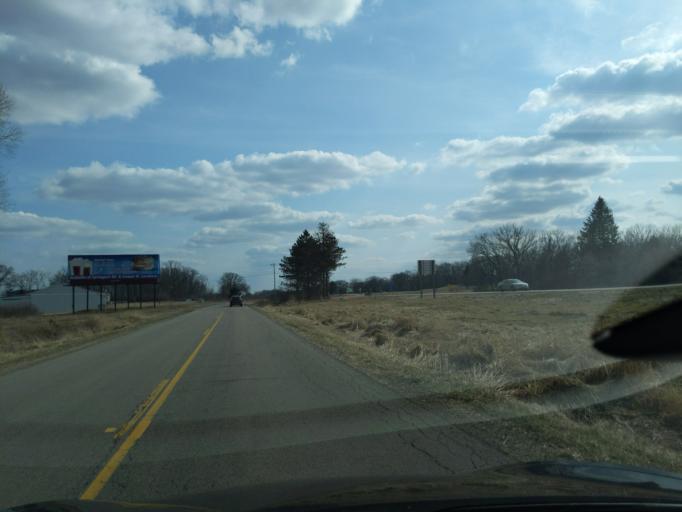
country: US
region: Michigan
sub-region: Ingham County
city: Leslie
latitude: 42.3693
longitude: -84.4284
